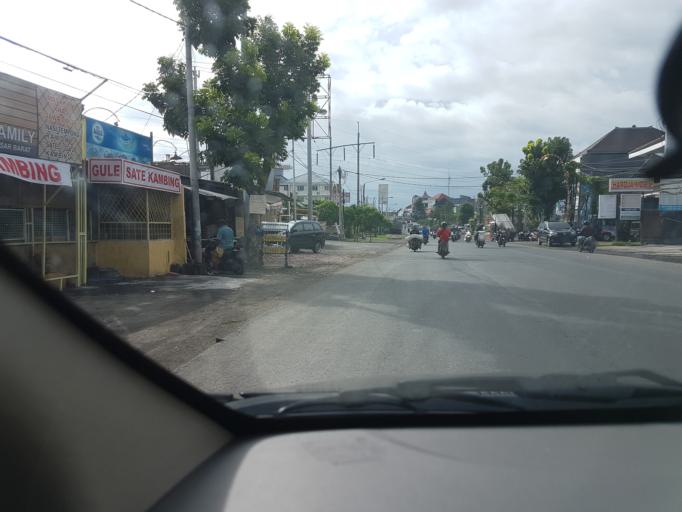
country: ID
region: Bali
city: Karyadharma
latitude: -8.6786
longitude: 115.1870
